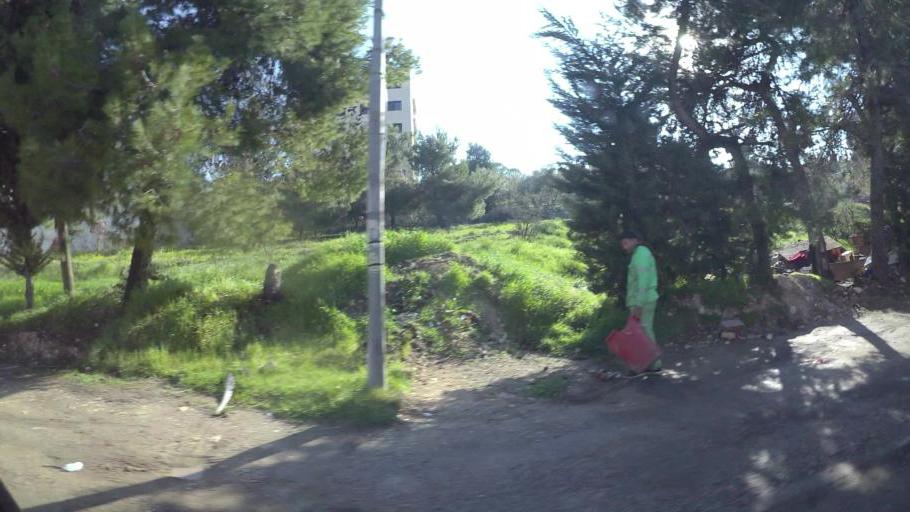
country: JO
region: Amman
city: Al Jubayhah
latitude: 32.0101
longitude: 35.8499
